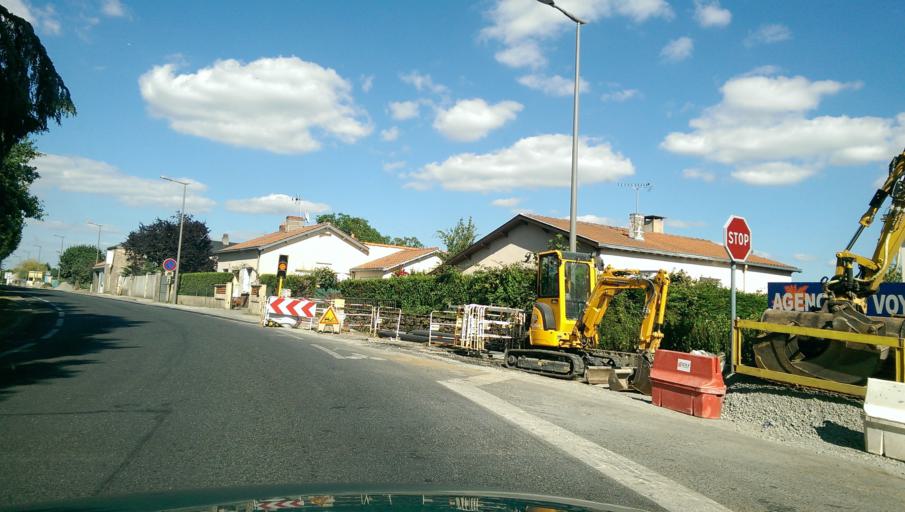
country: FR
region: Pays de la Loire
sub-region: Departement de la Vendee
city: Rocheserviere
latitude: 46.9398
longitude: -1.5071
